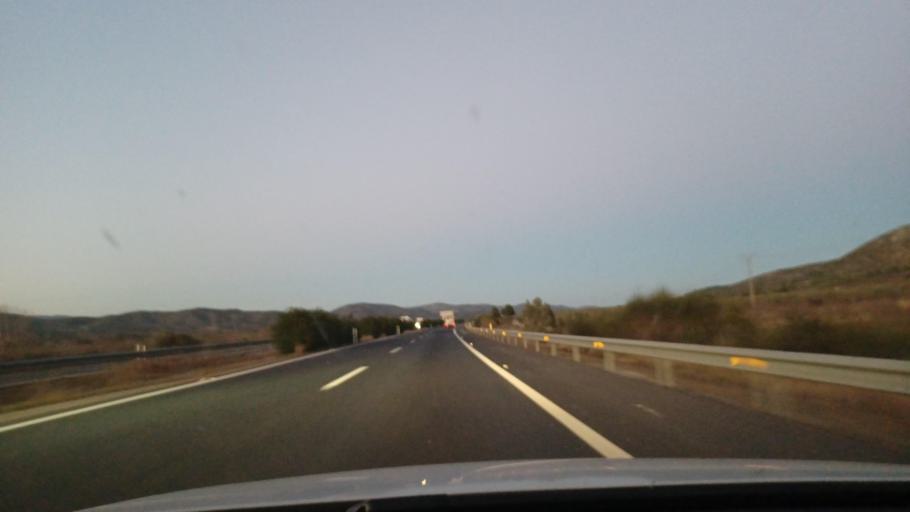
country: ES
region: Valencia
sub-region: Provincia de Castello
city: Alcala de Xivert
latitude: 40.3045
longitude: 0.2377
